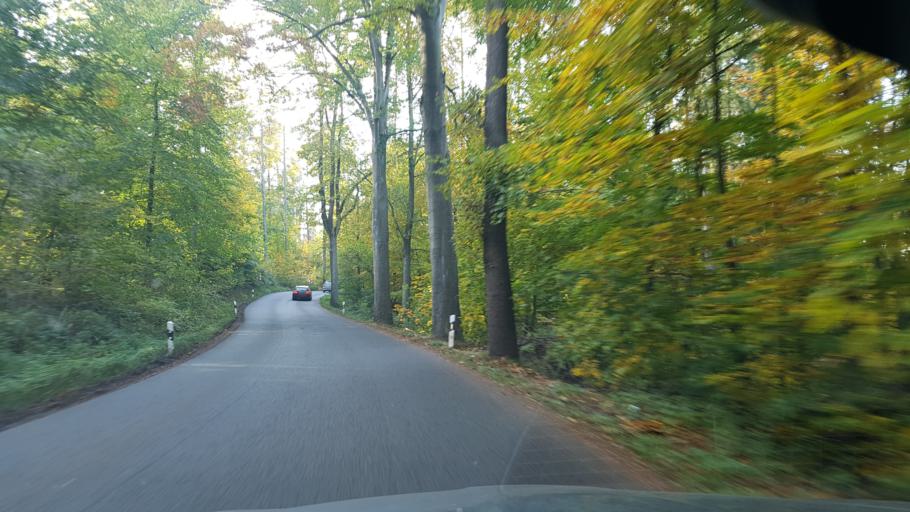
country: DE
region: Saxony
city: Struppen
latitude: 50.9267
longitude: 14.0448
